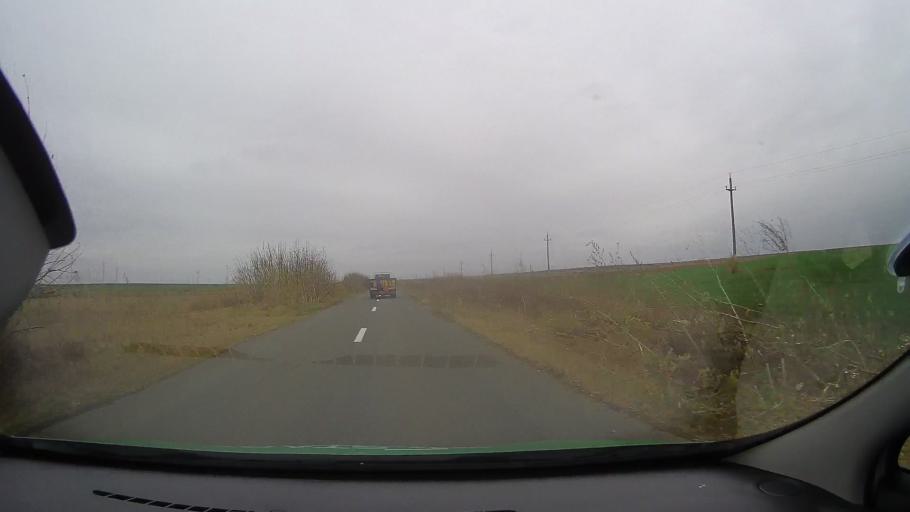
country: RO
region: Constanta
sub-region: Comuna Targusor
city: Targusor
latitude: 44.4671
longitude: 28.3930
